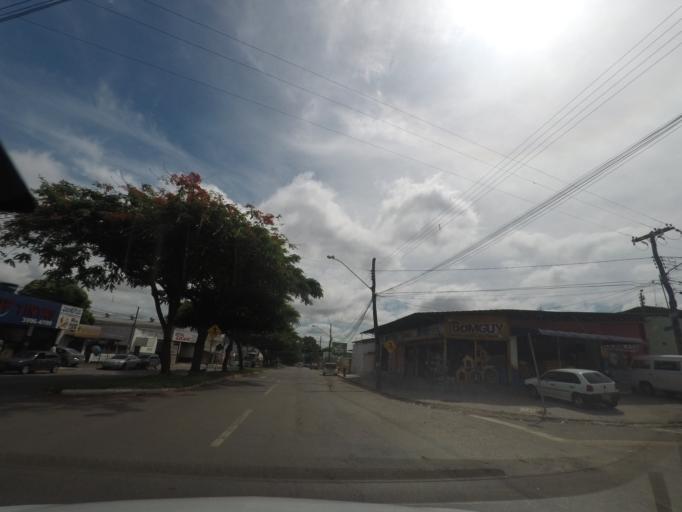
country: BR
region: Goias
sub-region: Goiania
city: Goiania
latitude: -16.6679
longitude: -49.2185
